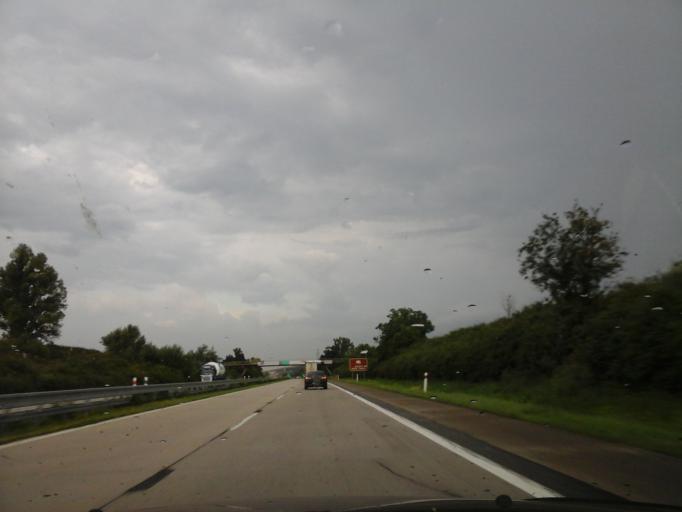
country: CZ
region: South Moravian
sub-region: Okres Brno-Venkov
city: Blucina
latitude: 49.0769
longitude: 16.6604
